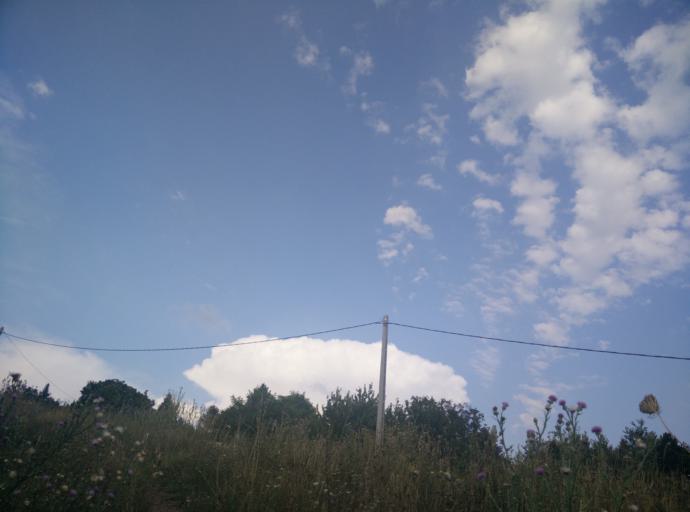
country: HU
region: Pest
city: Paty
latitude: 47.5021
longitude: 18.8475
